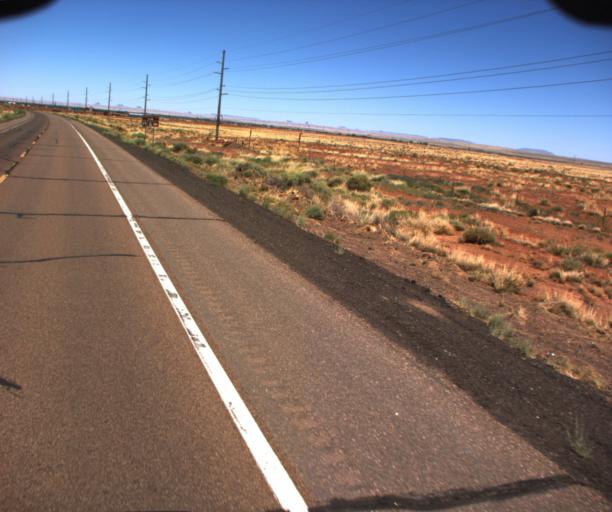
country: US
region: Arizona
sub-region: Navajo County
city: Winslow
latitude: 34.9974
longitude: -110.7062
